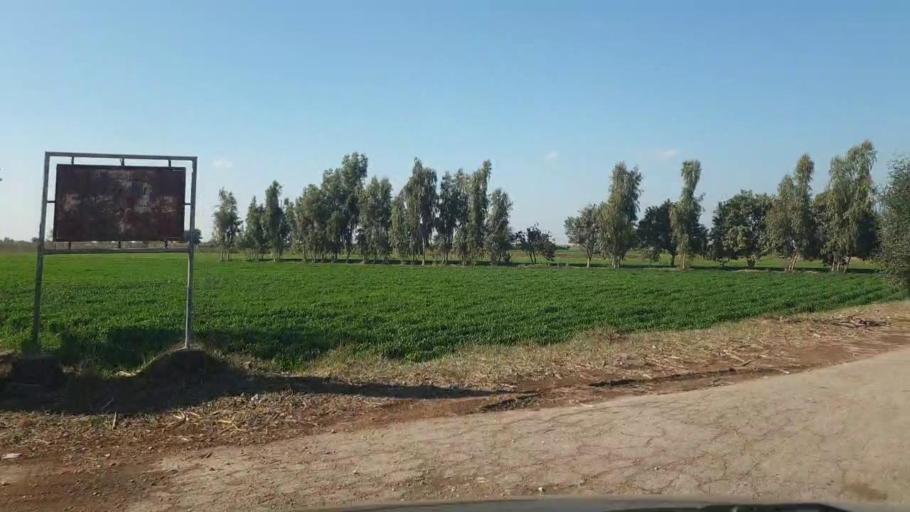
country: PK
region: Sindh
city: Shahdadpur
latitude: 25.9110
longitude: 68.5345
